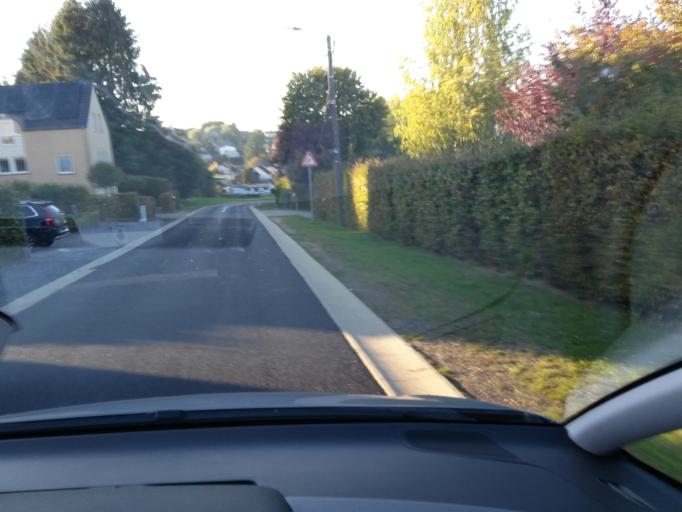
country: BE
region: Wallonia
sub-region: Province du Luxembourg
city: Arlon
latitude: 49.6929
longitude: 5.8238
